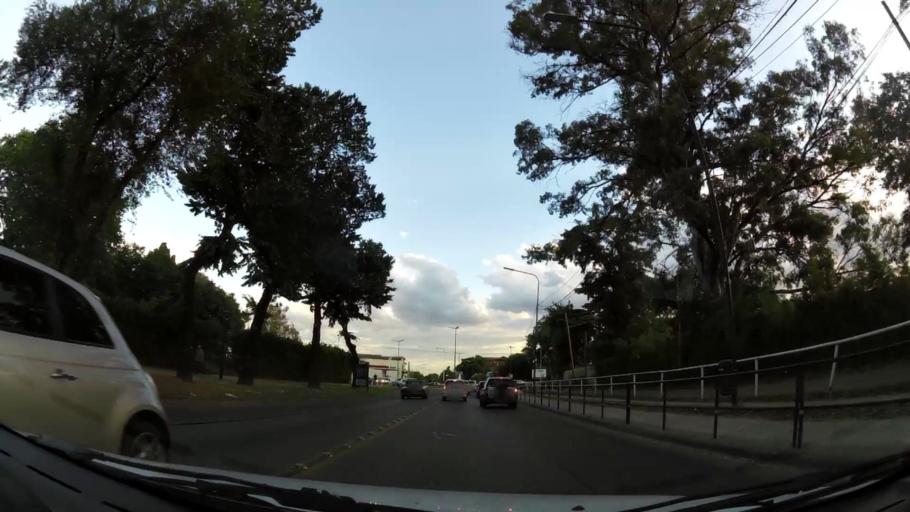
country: AR
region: Buenos Aires
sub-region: Partido de San Isidro
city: San Isidro
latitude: -34.4888
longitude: -58.5252
